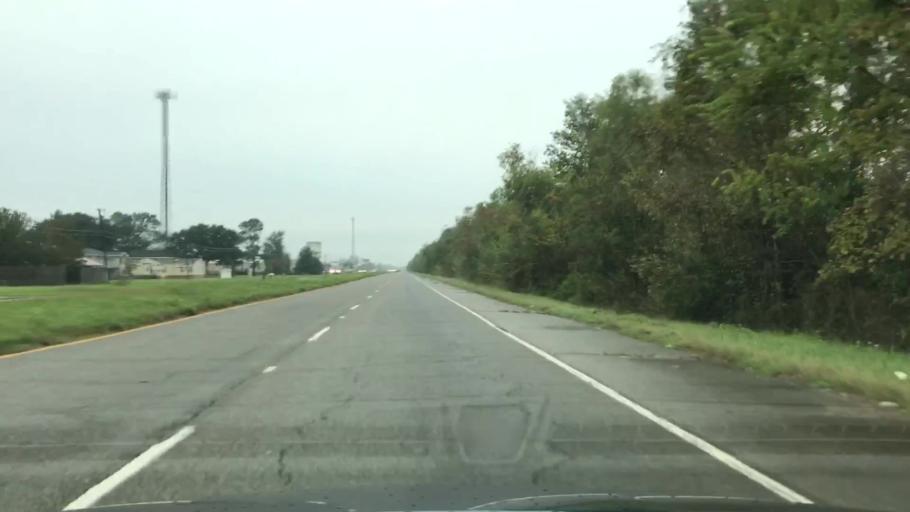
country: US
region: Louisiana
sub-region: Saint Charles Parish
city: Des Allemands
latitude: 29.8167
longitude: -90.4874
